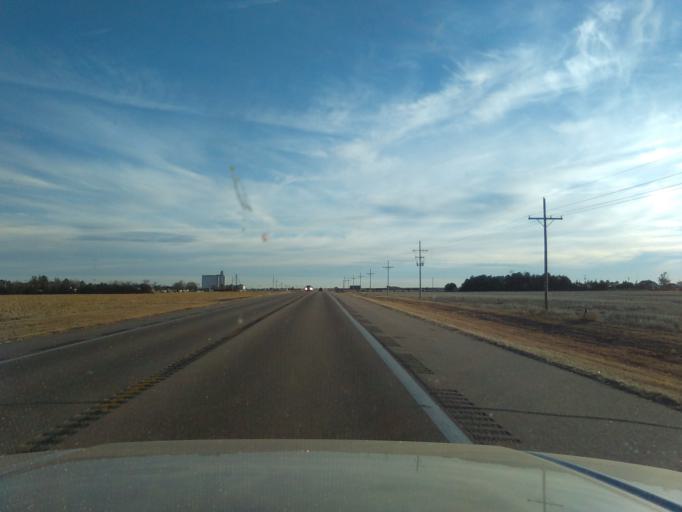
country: US
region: Kansas
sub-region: Logan County
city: Oakley
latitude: 39.1382
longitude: -100.8682
